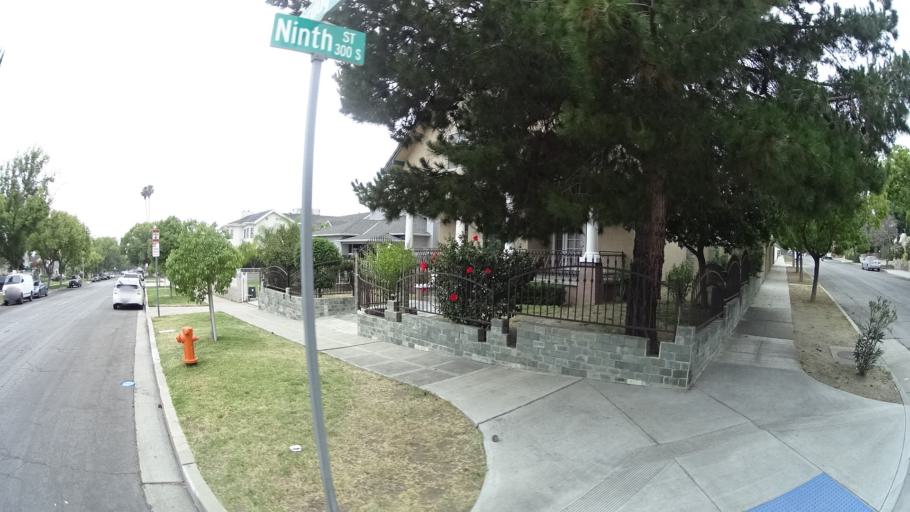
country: US
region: California
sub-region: Los Angeles County
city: Burbank
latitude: 34.1868
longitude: -118.2973
